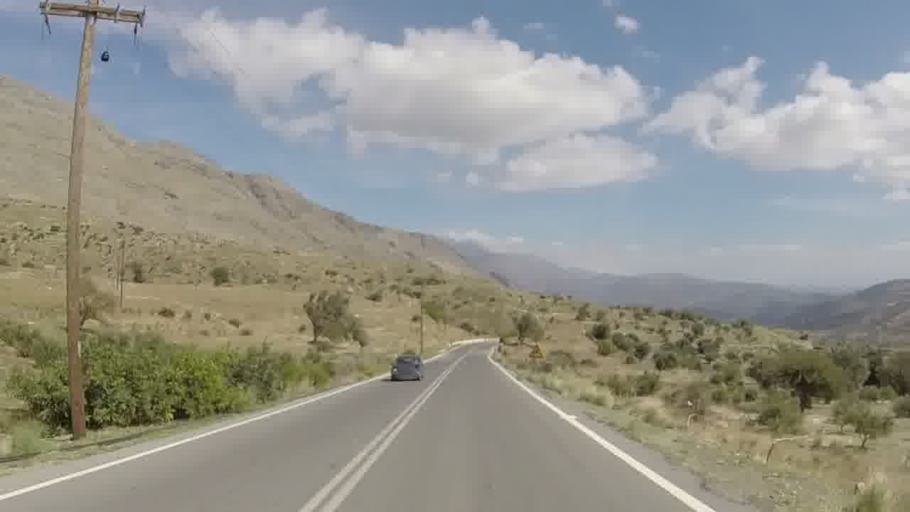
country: GR
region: Crete
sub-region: Nomos Rethymnis
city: Agia Galini
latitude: 35.1484
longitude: 24.6299
